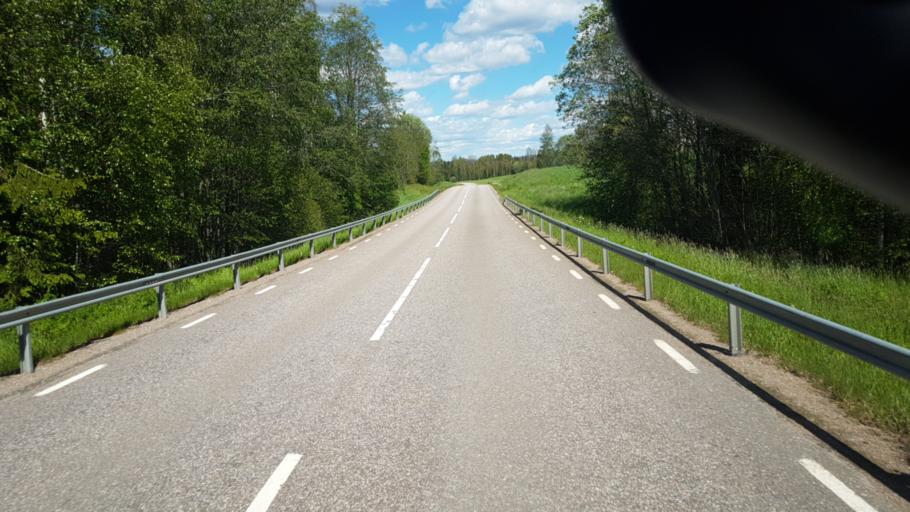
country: SE
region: Vaermland
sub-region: Arvika Kommun
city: Arvika
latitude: 59.6415
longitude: 12.8884
